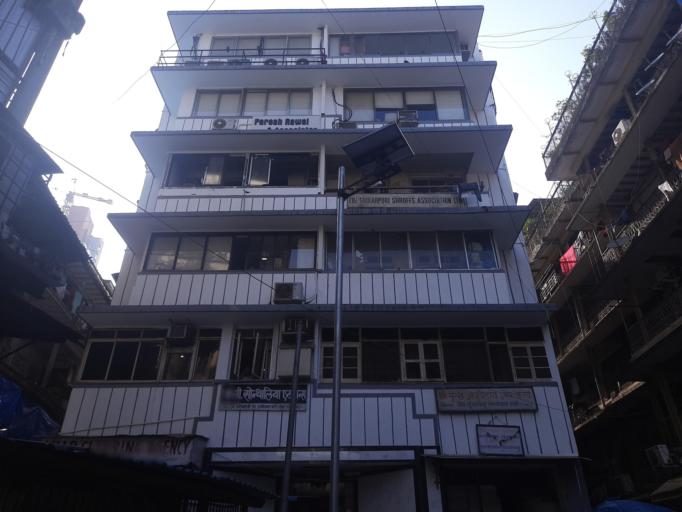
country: IN
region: Maharashtra
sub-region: Raigarh
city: Uran
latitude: 18.9483
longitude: 72.8287
